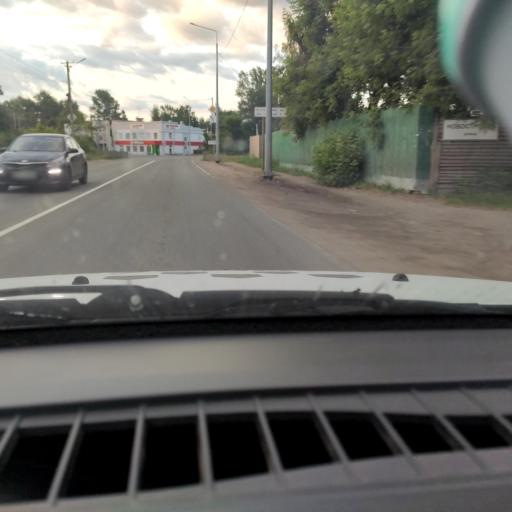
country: RU
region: Kirov
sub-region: Kirovo-Chepetskiy Rayon
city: Kirov
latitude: 58.6133
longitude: 49.7446
